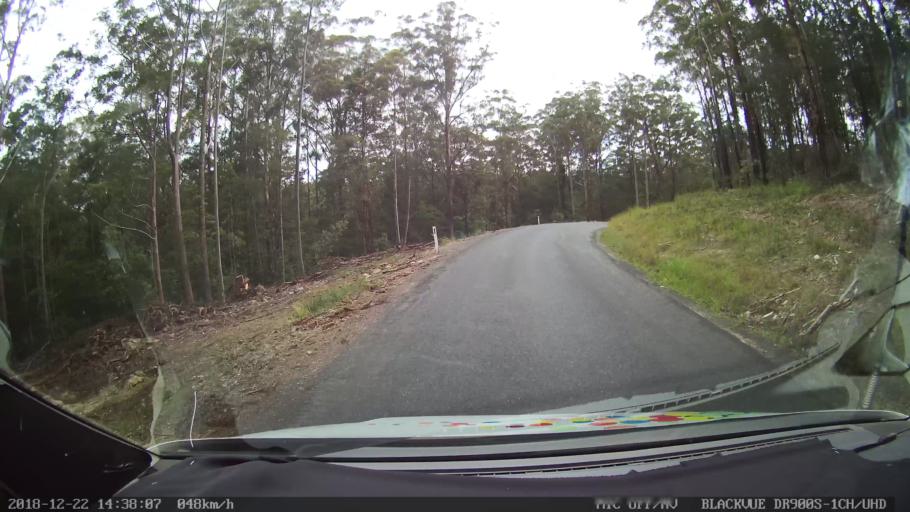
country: AU
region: New South Wales
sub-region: Bellingen
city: Dorrigo
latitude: -30.1368
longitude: 152.5997
